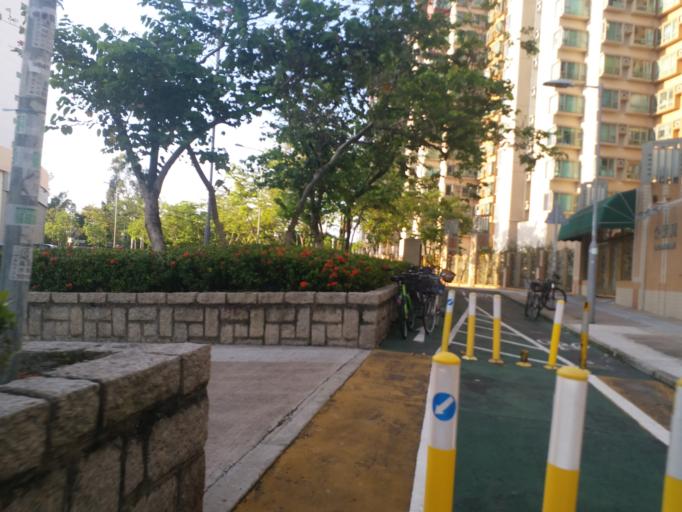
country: HK
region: Yuen Long
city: Yuen Long Kau Hui
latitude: 22.4502
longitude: 114.0317
